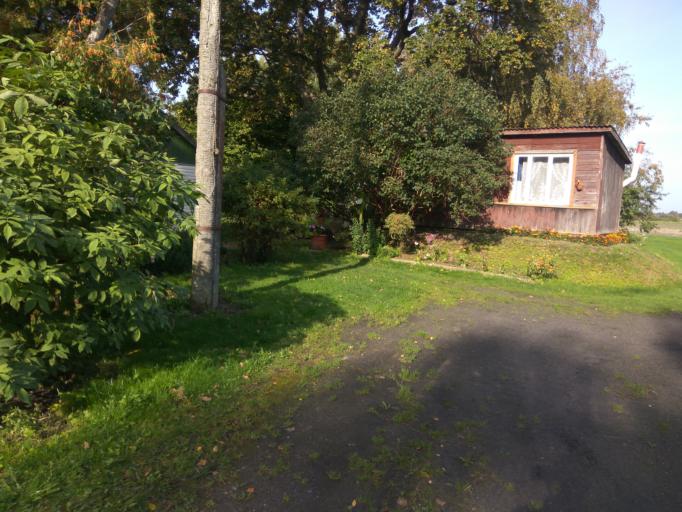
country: LV
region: Ventspils
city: Ventspils
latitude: 57.3563
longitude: 21.6400
